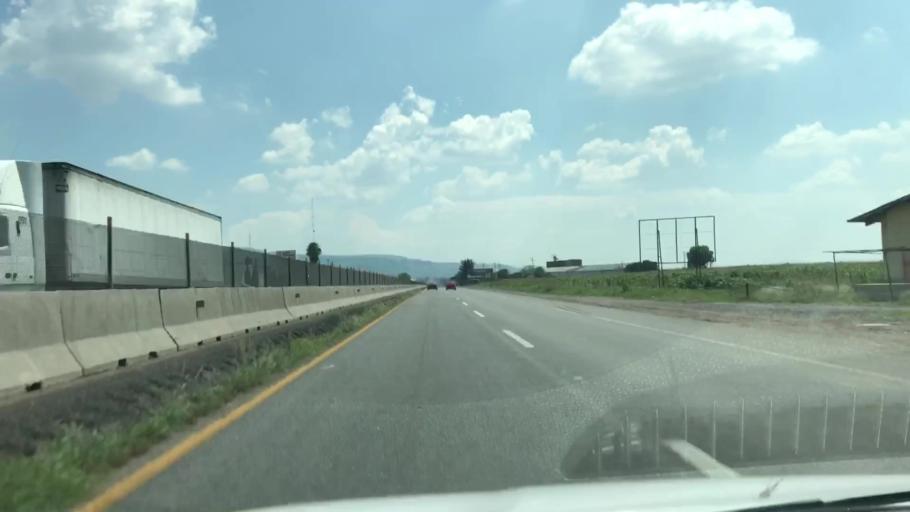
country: MX
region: Guanajuato
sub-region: Abasolo
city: San Bernardo Pena Blanca
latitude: 20.4929
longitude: -101.4861
